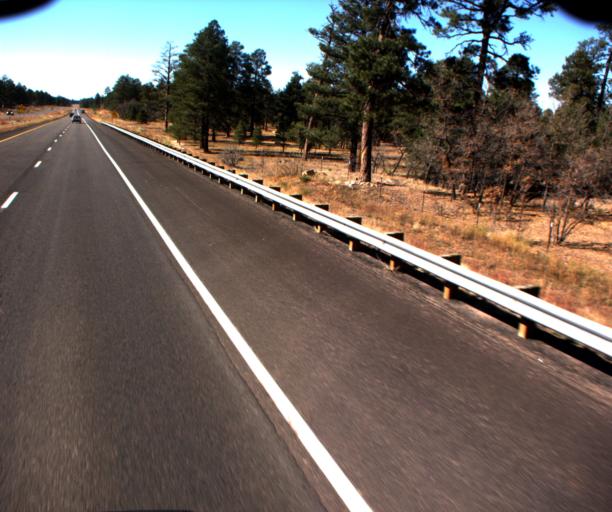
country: US
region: Arizona
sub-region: Apache County
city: Saint Michaels
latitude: 35.6795
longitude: -109.2077
